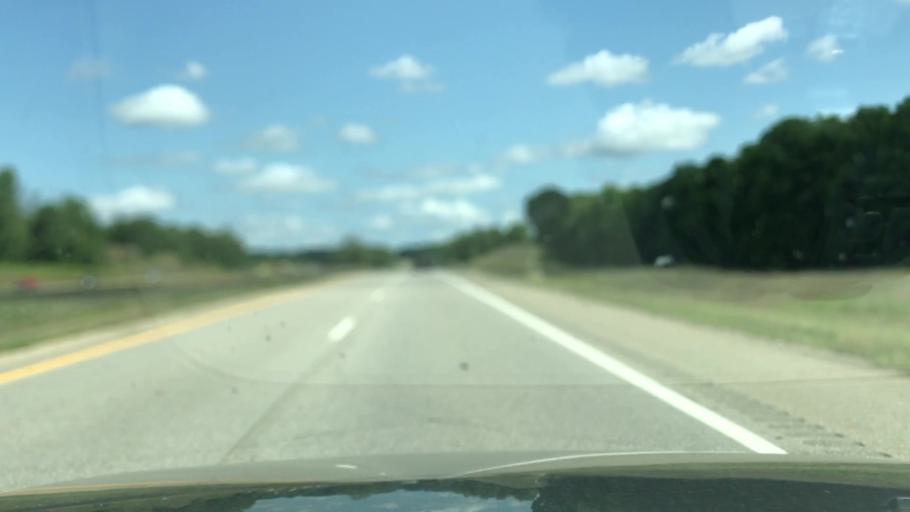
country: US
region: Michigan
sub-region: Osceola County
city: Reed City
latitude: 43.7937
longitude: -85.5338
